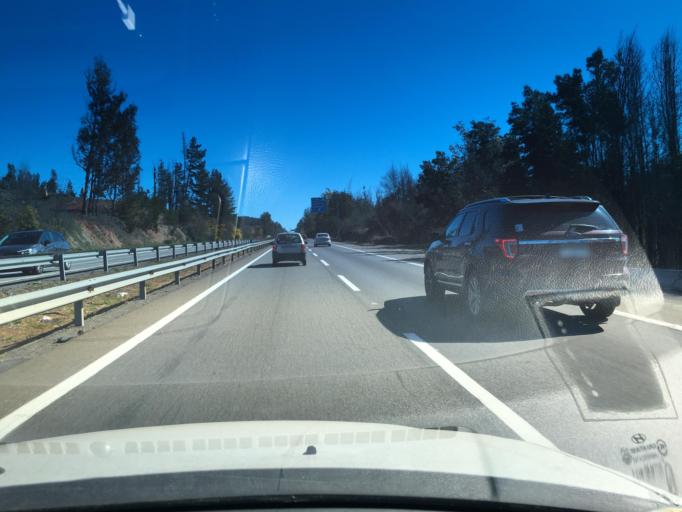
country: CL
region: Valparaiso
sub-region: Provincia de Marga Marga
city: Quilpue
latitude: -33.1703
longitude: -71.5244
